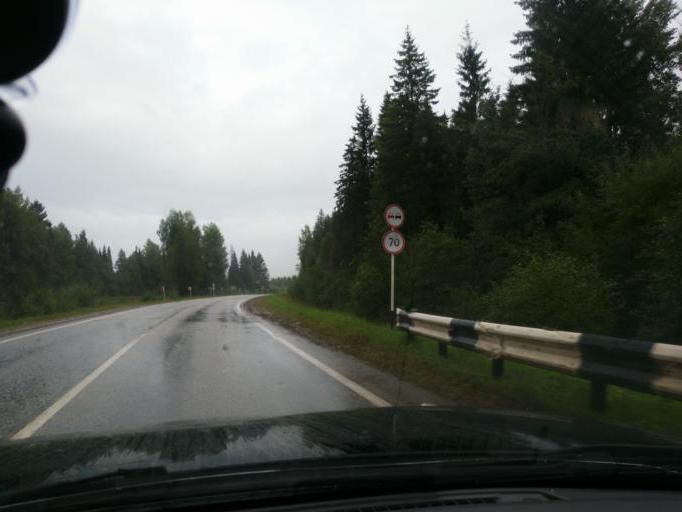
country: RU
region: Perm
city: Osa
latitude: 57.3891
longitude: 55.6086
